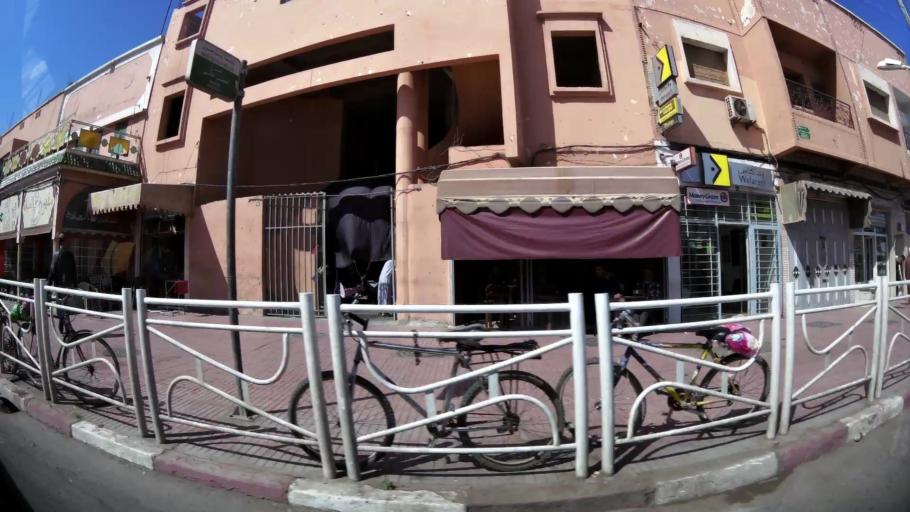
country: MA
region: Souss-Massa-Draa
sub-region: Inezgane-Ait Mellou
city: Inezgane
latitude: 30.3481
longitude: -9.5033
